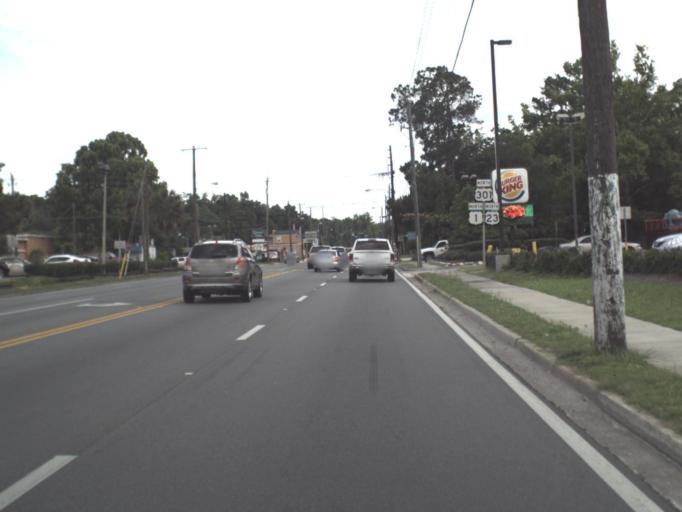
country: US
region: Florida
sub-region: Nassau County
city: Callahan
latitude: 30.5639
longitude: -81.8300
